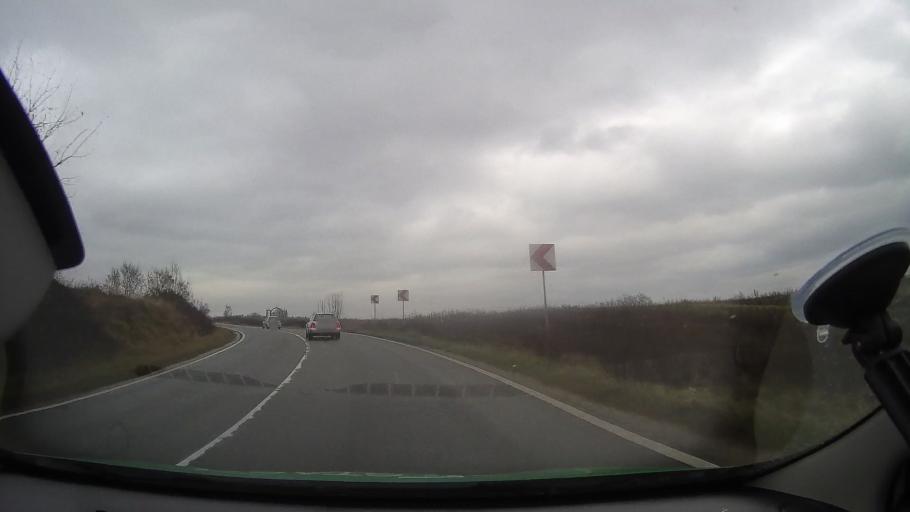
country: RO
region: Arad
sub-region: Comuna Almas
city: Almas
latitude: 46.2825
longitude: 22.2430
